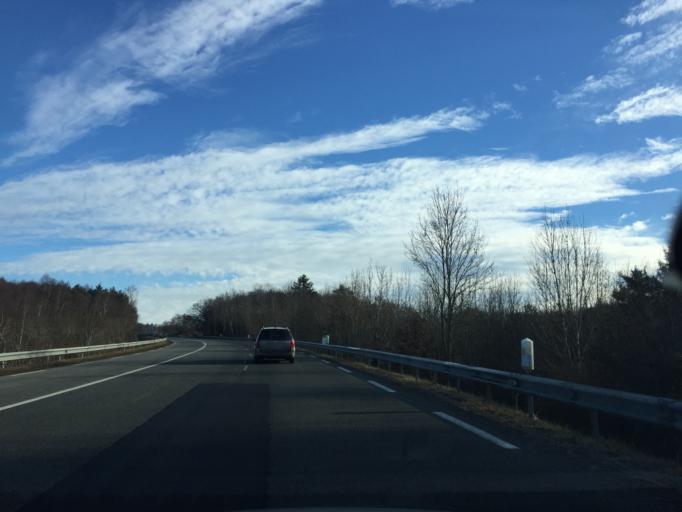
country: FR
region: Auvergne
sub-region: Departement du Puy-de-Dome
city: Gelles
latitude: 45.8537
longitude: 2.6802
